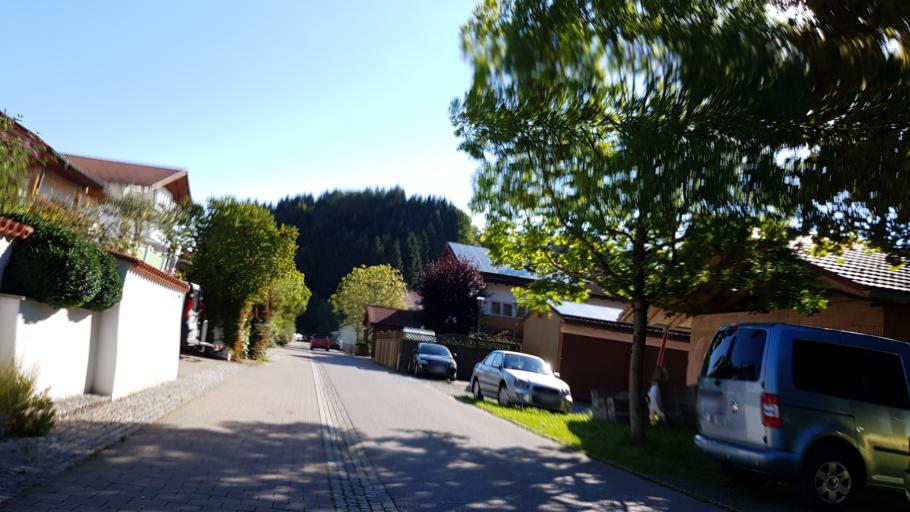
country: DE
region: Bavaria
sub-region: Swabia
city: Fuessen
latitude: 47.5734
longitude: 10.6903
